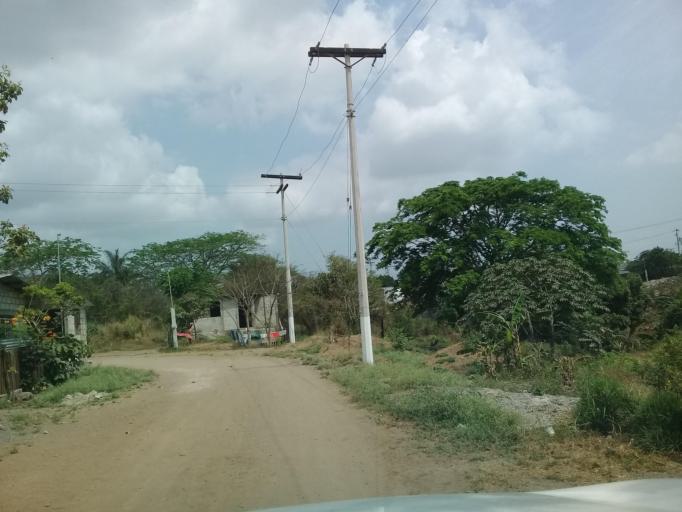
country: MX
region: Veracruz
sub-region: Veracruz
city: Las Amapolas
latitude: 19.1367
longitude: -96.2397
